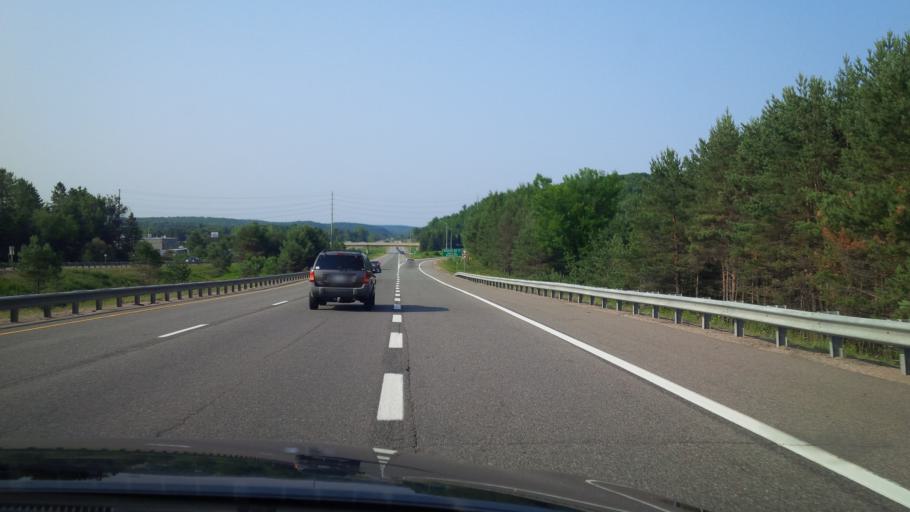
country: CA
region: Ontario
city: Huntsville
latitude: 45.3376
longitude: -79.2351
